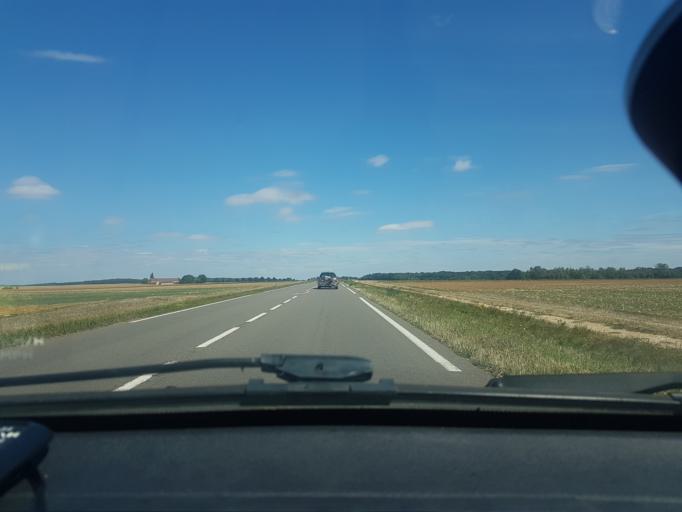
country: FR
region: Bourgogne
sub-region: Departement de la Cote-d'Or
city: Arc-sur-Tille
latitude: 47.3493
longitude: 5.2014
